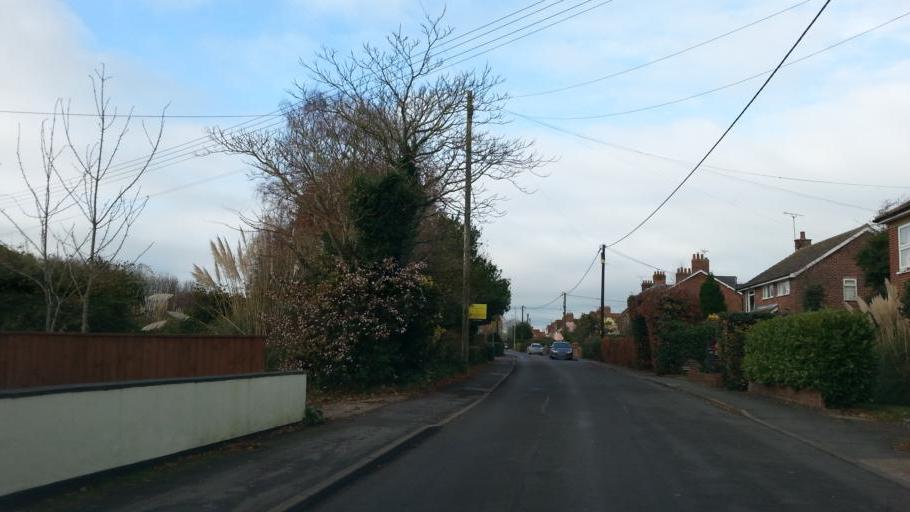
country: GB
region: England
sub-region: Suffolk
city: Framlingham
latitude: 52.2271
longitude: 1.3339
